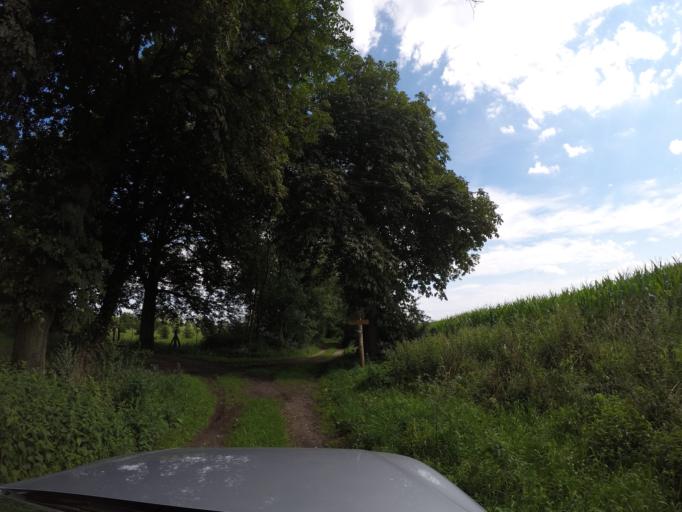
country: DE
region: Mecklenburg-Vorpommern
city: Mollenhagen
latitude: 53.4821
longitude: 12.9427
